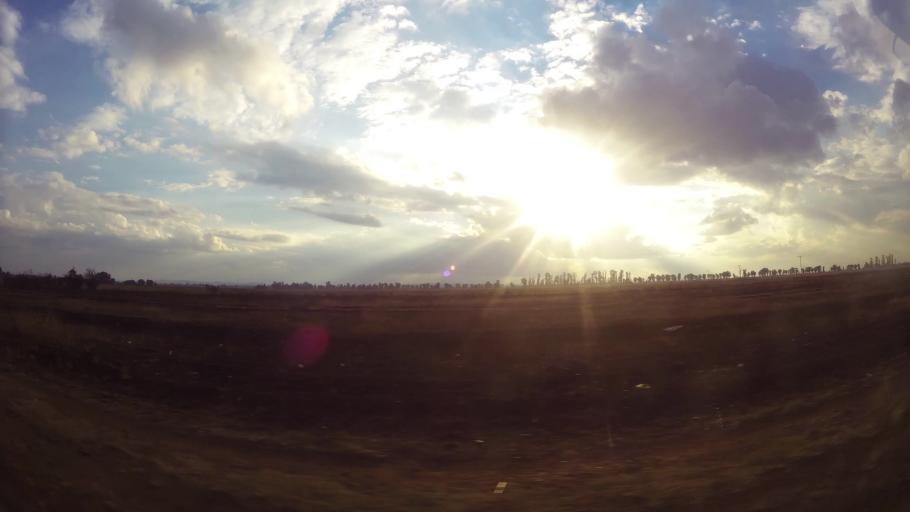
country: ZA
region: Gauteng
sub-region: Sedibeng District Municipality
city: Vanderbijlpark
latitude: -26.6564
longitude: 27.8019
